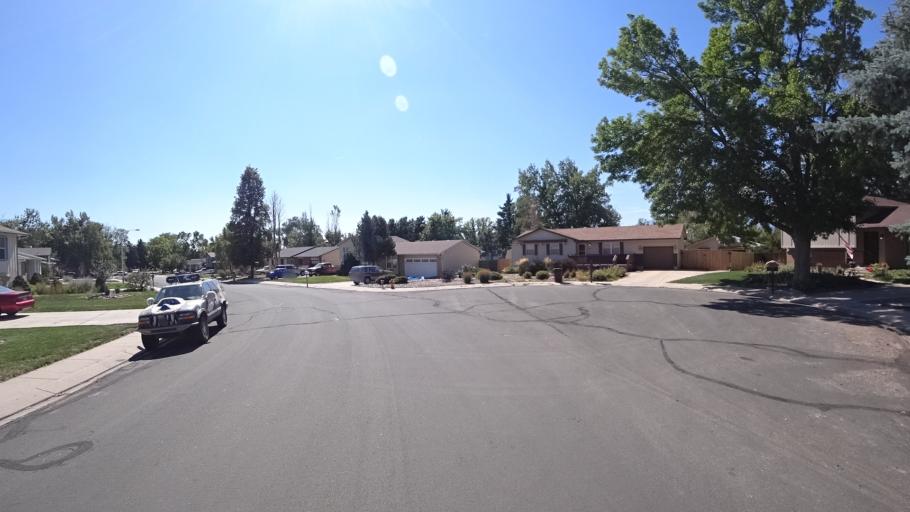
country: US
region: Colorado
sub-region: El Paso County
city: Cimarron Hills
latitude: 38.9051
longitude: -104.7626
